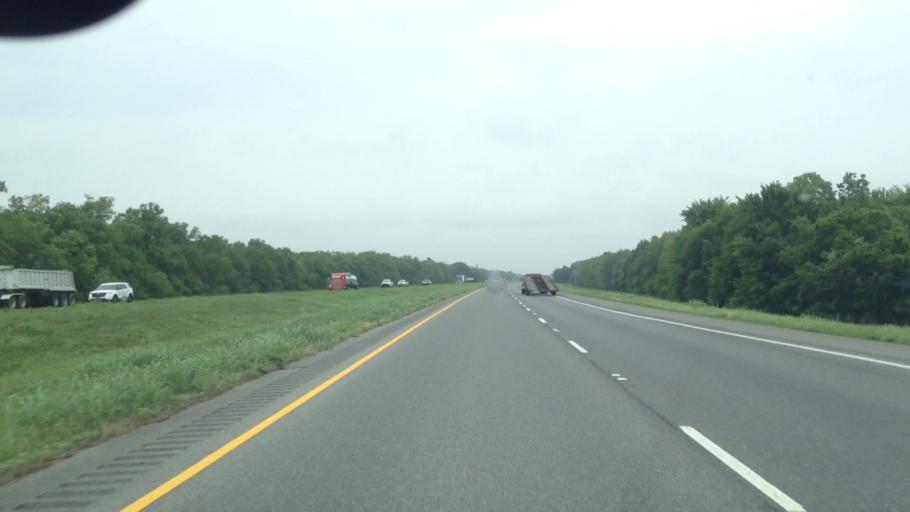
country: US
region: Louisiana
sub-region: Evangeline Parish
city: Ville Platte
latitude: 30.7289
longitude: -92.1255
